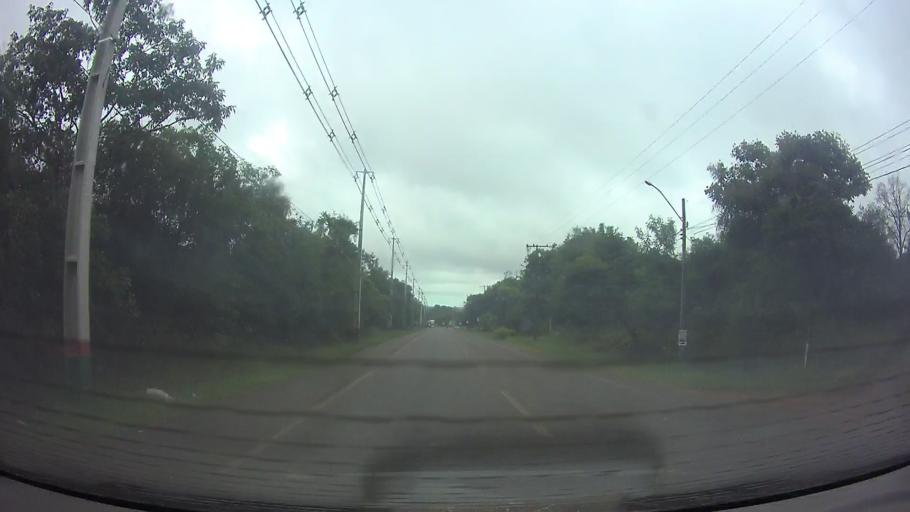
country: PY
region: Cordillera
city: Altos
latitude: -25.2711
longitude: -57.2564
